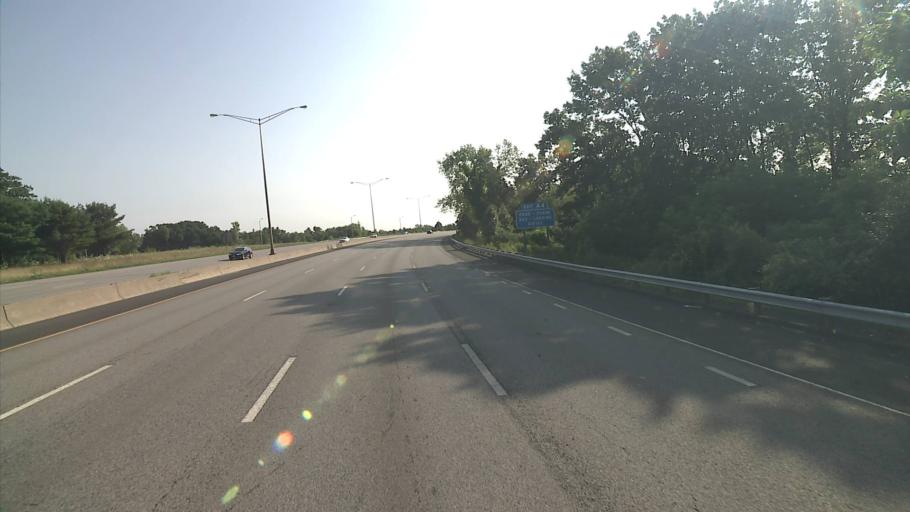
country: US
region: Connecticut
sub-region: Hartford County
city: Windsor Locks
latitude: 41.9141
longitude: -72.6299
